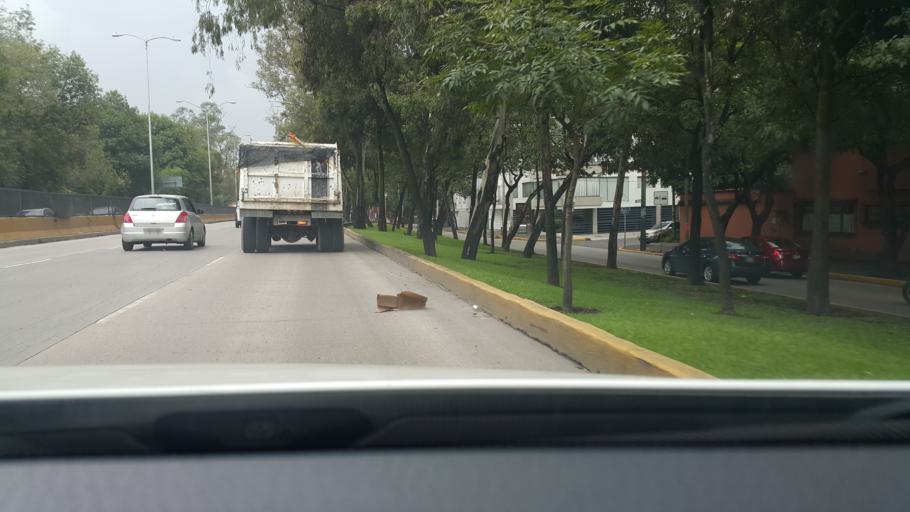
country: MX
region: Mexico City
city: Coyoacan
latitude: 19.3580
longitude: -99.1666
